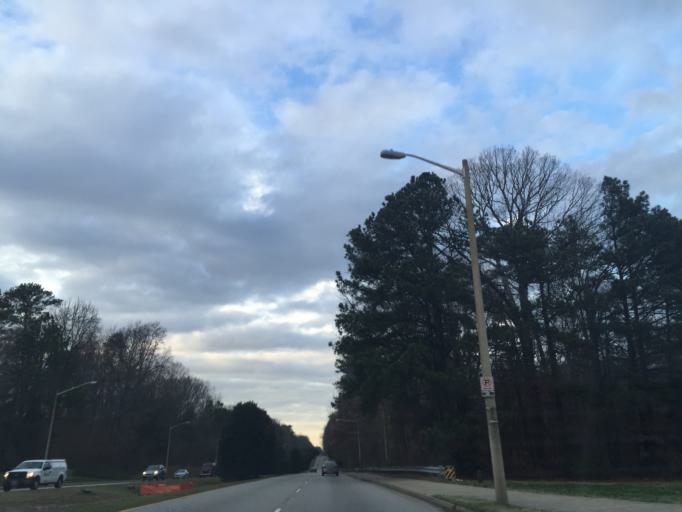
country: US
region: Virginia
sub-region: City of Newport News
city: Newport News
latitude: 37.0925
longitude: -76.5038
